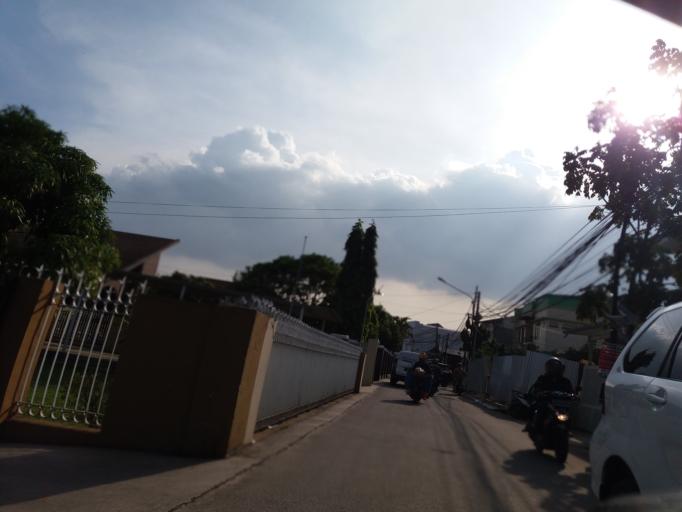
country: ID
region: West Java
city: Bandung
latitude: -6.9517
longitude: 107.6279
